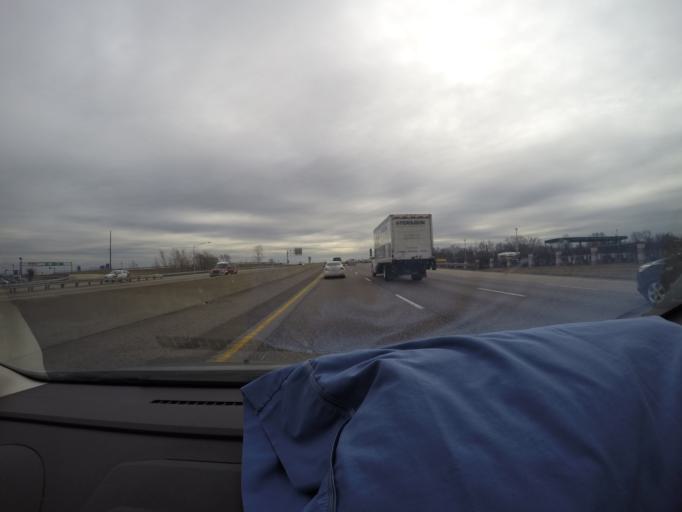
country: US
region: Missouri
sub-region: Saint Louis County
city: Saint Ann
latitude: 38.7431
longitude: -90.3880
